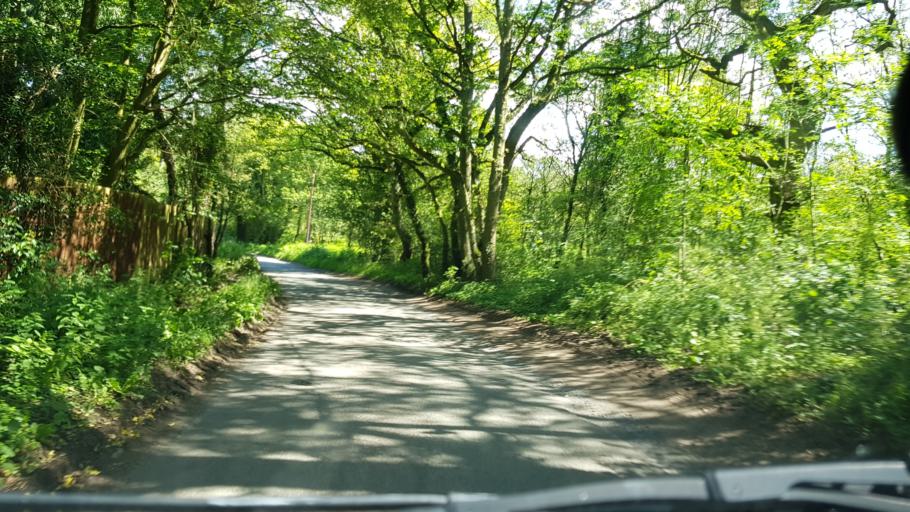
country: GB
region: England
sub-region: Worcestershire
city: Kidderminster
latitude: 52.4396
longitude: -2.2591
